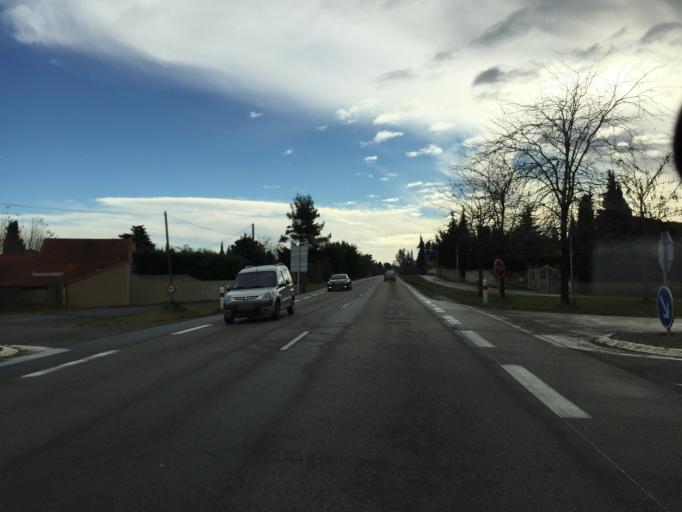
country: FR
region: Provence-Alpes-Cote d'Azur
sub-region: Departement du Vaucluse
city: Velleron
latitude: 43.9359
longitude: 5.0297
